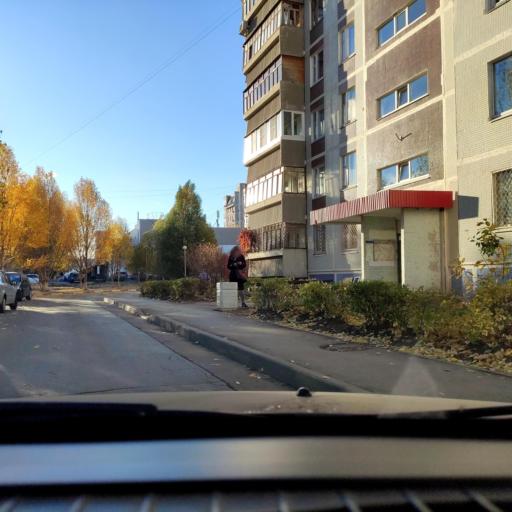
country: RU
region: Samara
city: Tol'yatti
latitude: 53.5433
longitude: 49.3627
